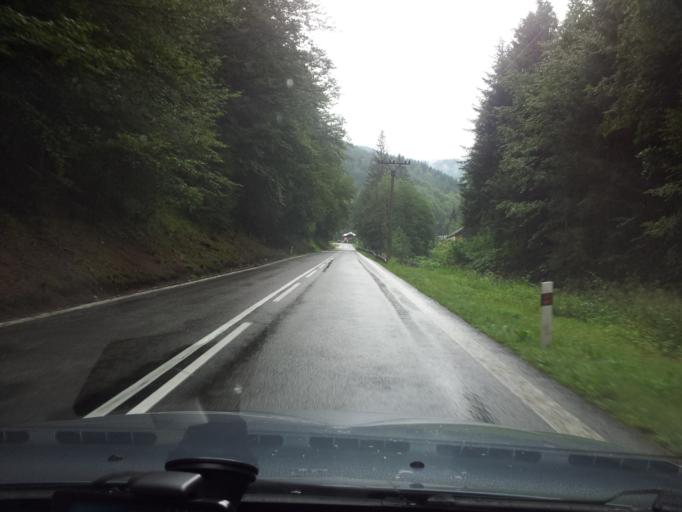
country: SK
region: Banskobystricky
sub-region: Okres Banska Bystrica
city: Brezno
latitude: 48.8895
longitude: 19.6829
